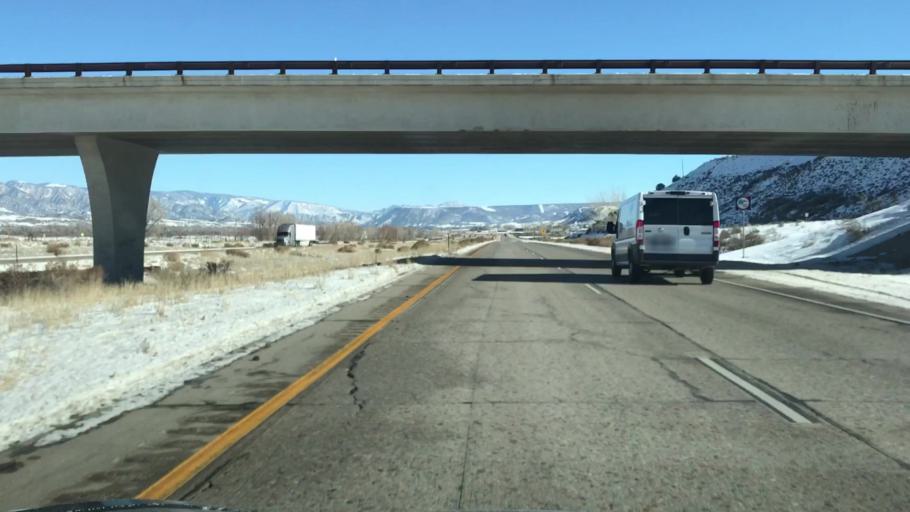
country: US
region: Colorado
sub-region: Garfield County
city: Silt
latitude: 39.5318
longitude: -107.7131
